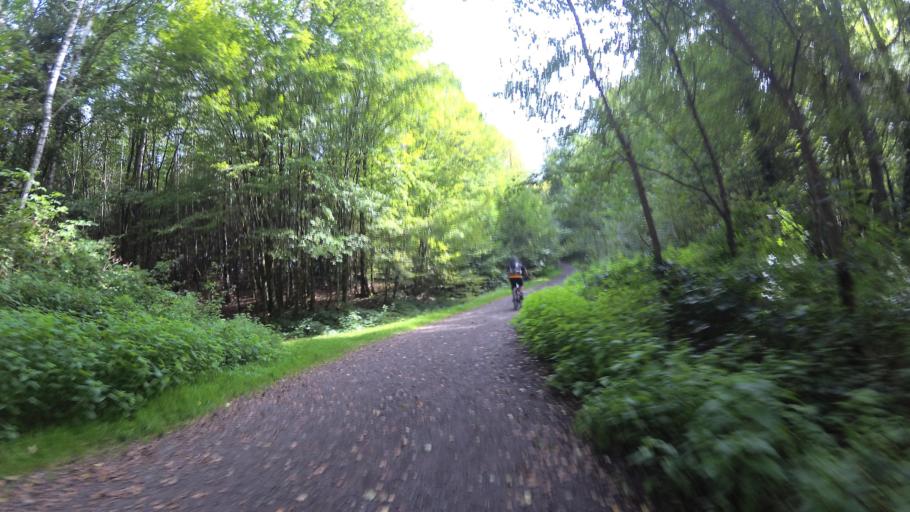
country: DE
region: Saarland
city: Friedrichsthal
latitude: 49.3046
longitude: 7.0943
